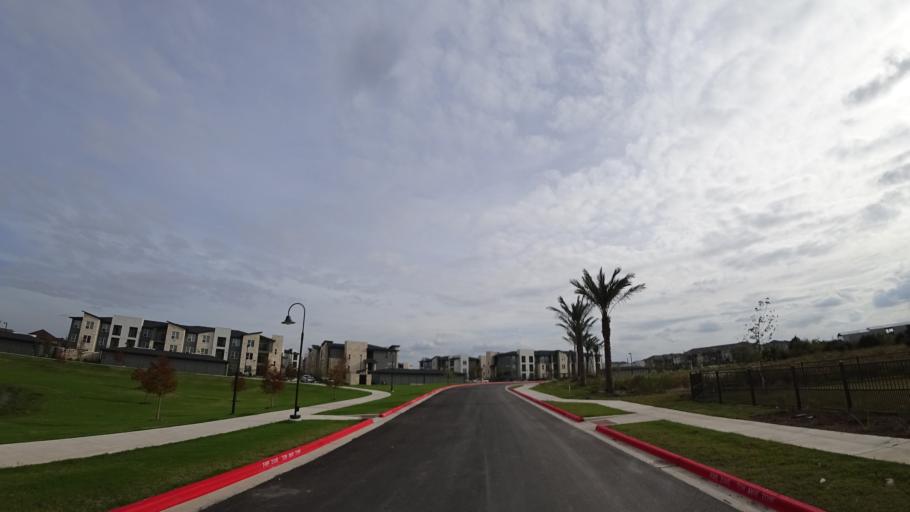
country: US
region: Texas
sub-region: Travis County
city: Wells Branch
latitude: 30.4321
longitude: -97.6660
